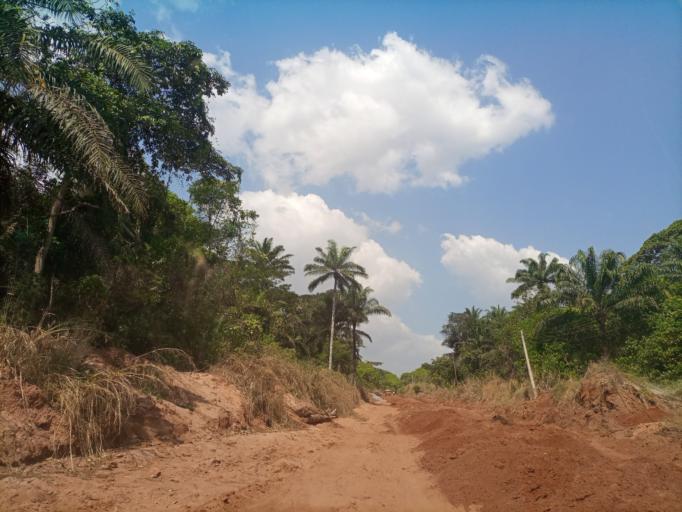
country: NG
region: Enugu
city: Obollo-Afor
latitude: 6.8849
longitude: 7.5211
